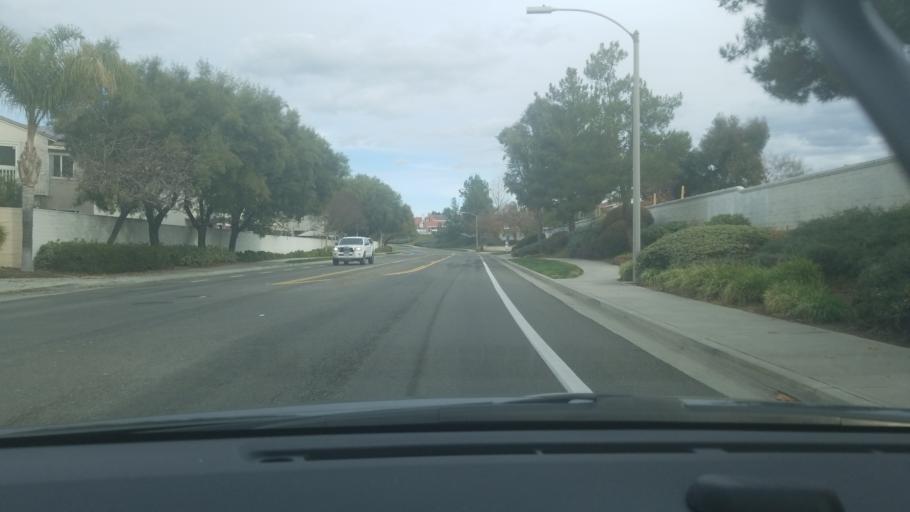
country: US
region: California
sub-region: Riverside County
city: Temecula
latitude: 33.4773
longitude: -117.0932
